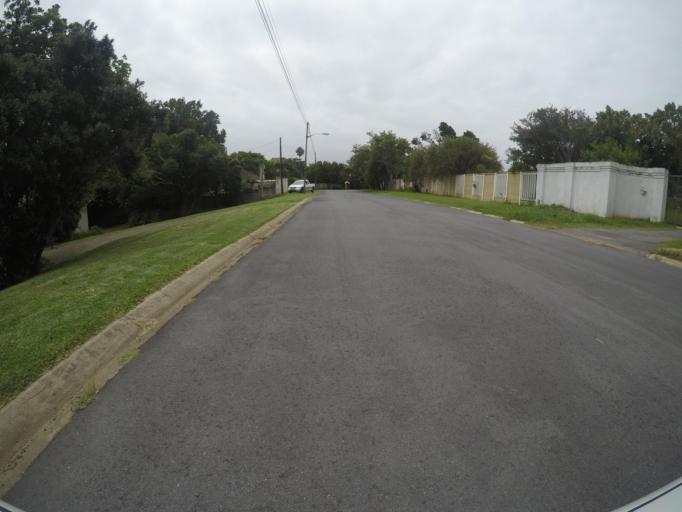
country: ZA
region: Eastern Cape
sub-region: Buffalo City Metropolitan Municipality
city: East London
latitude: -32.9779
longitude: 27.9413
